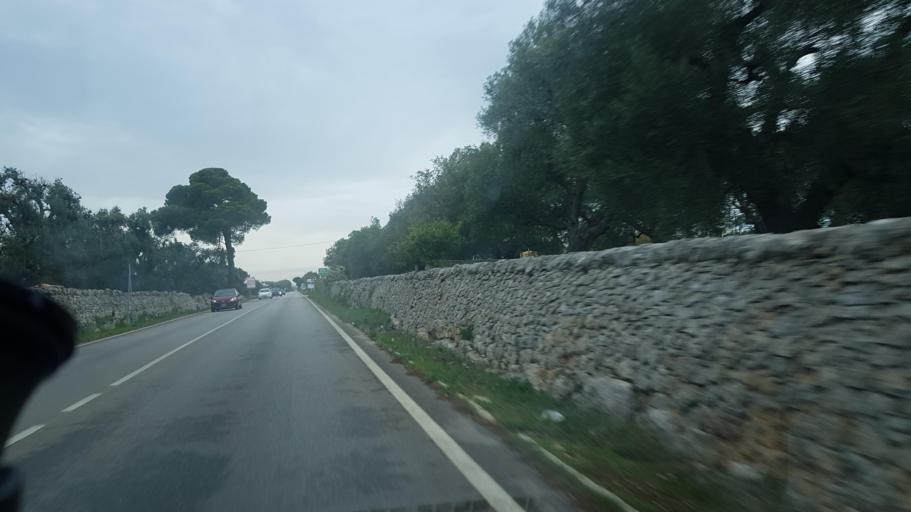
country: IT
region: Apulia
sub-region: Provincia di Brindisi
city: Carovigno
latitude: 40.7147
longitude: 17.6241
